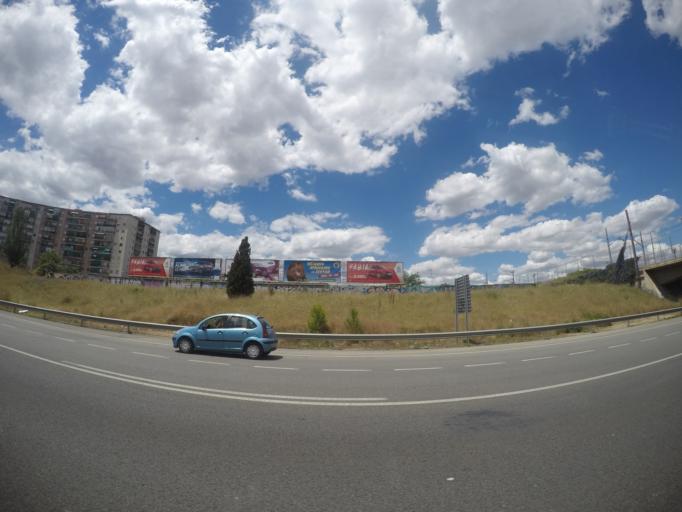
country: ES
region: Catalonia
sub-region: Provincia de Barcelona
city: Sant Adria de Besos
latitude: 41.4243
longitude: 2.2141
